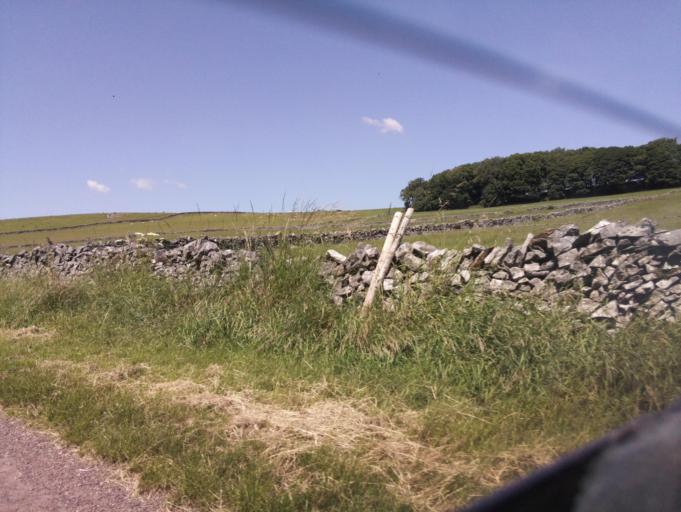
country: GB
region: England
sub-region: Derbyshire
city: Tideswell
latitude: 53.2758
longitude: -1.8361
